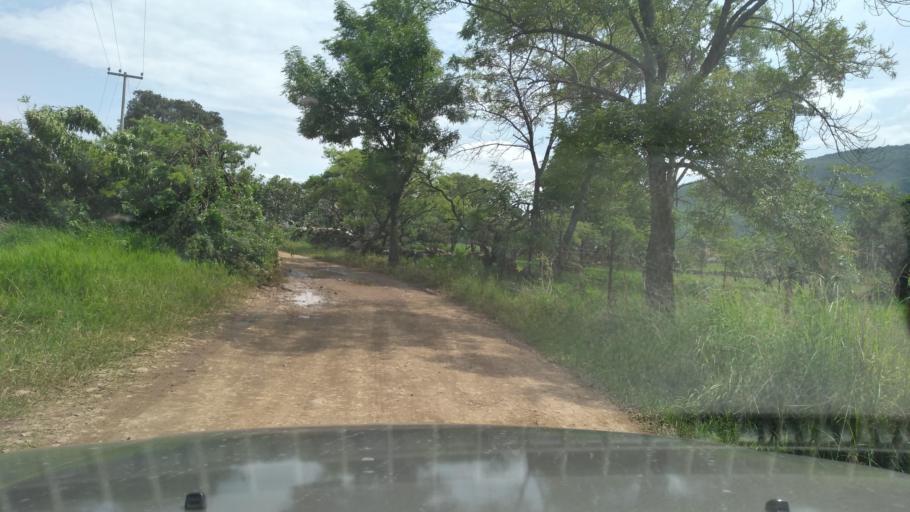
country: MX
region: Jalisco
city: Capilla de Guadalupe
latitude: 20.7471
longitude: -102.6324
